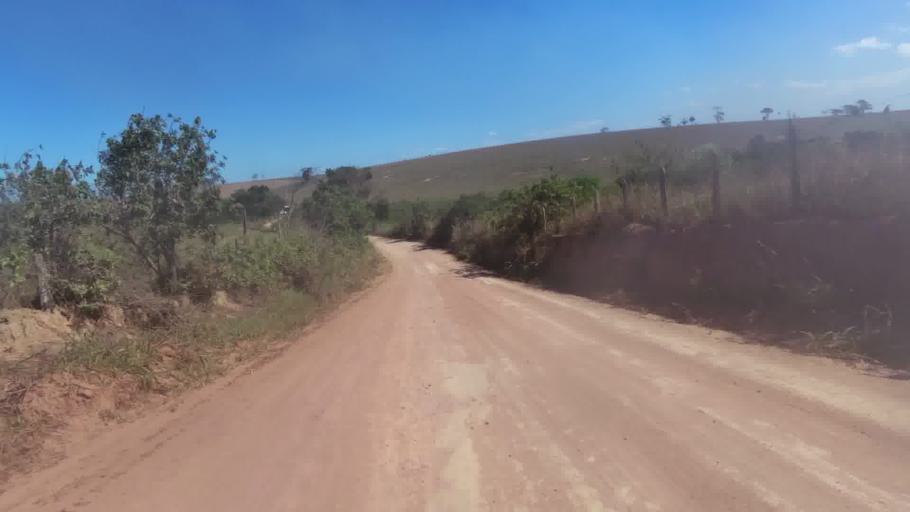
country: BR
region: Espirito Santo
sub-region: Marataizes
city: Marataizes
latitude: -21.1586
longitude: -40.9808
